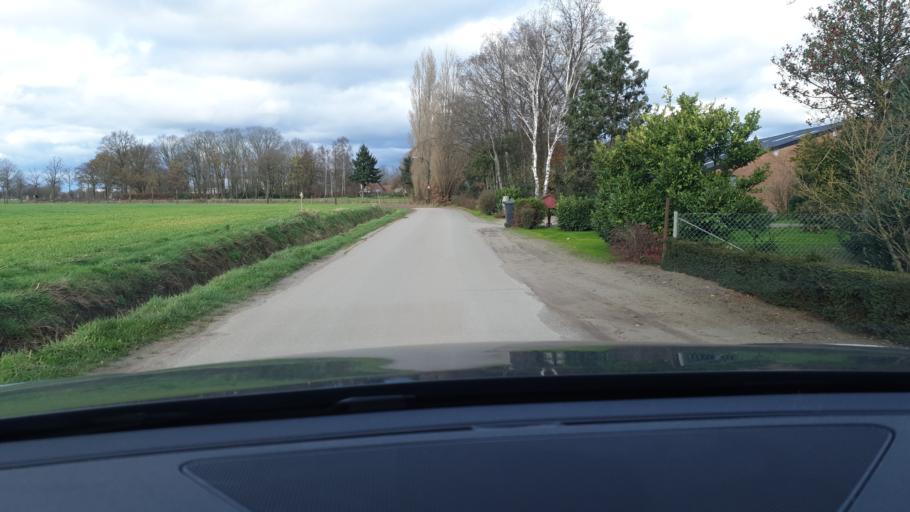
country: NL
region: North Brabant
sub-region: Gemeente Waalre
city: Waalre
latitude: 51.3795
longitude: 5.4329
